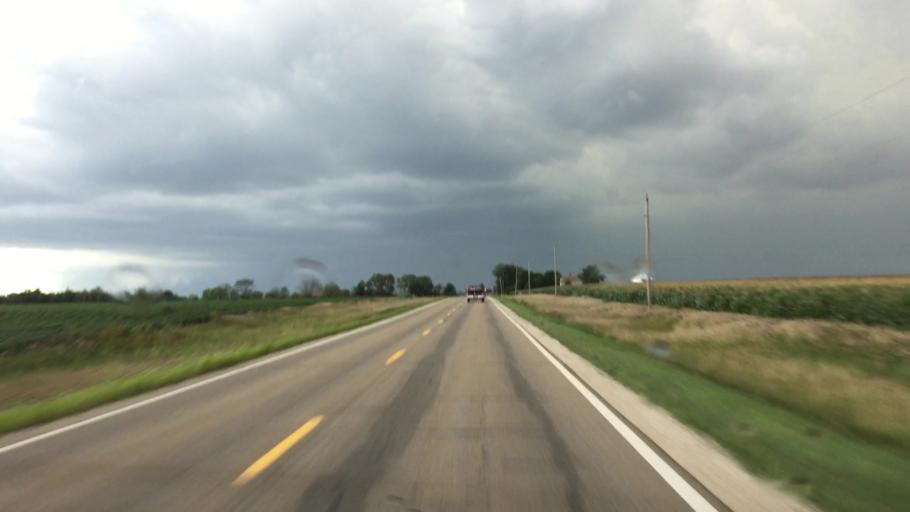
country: US
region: Iowa
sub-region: Henry County
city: New London
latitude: 40.7843
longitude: -91.5007
